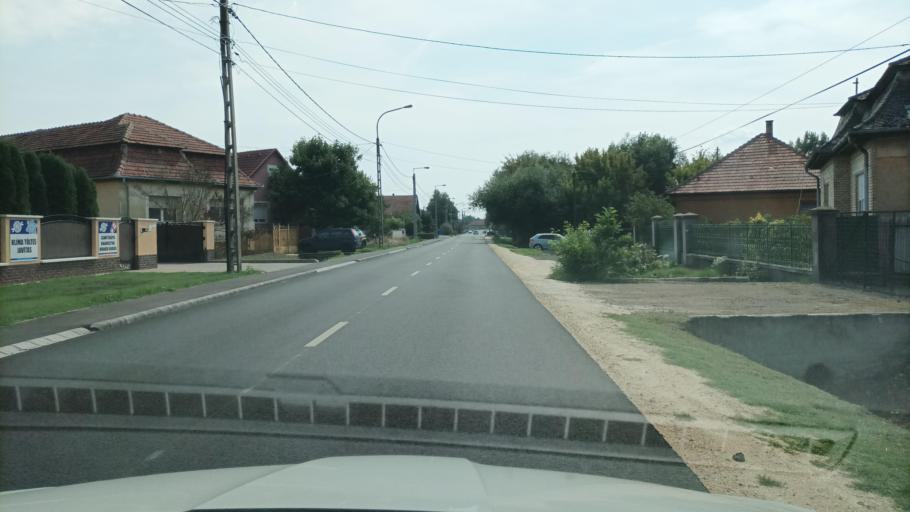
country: HU
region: Pest
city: Tura
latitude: 47.6197
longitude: 19.5977
